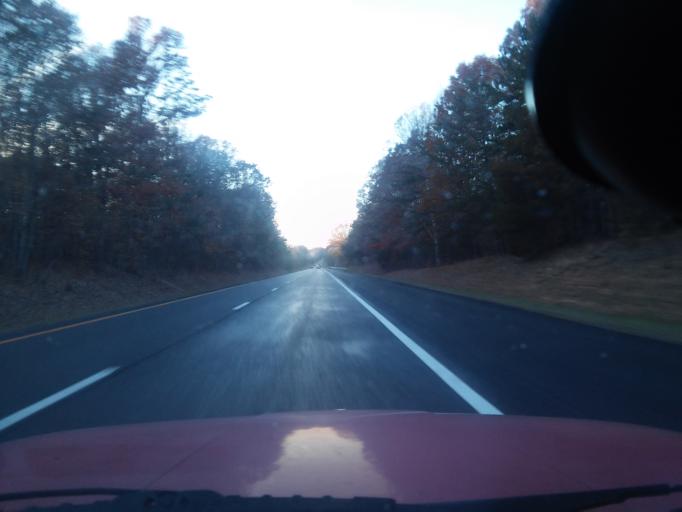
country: US
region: Virginia
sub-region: Louisa County
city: Louisa
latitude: 37.8626
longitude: -78.0027
